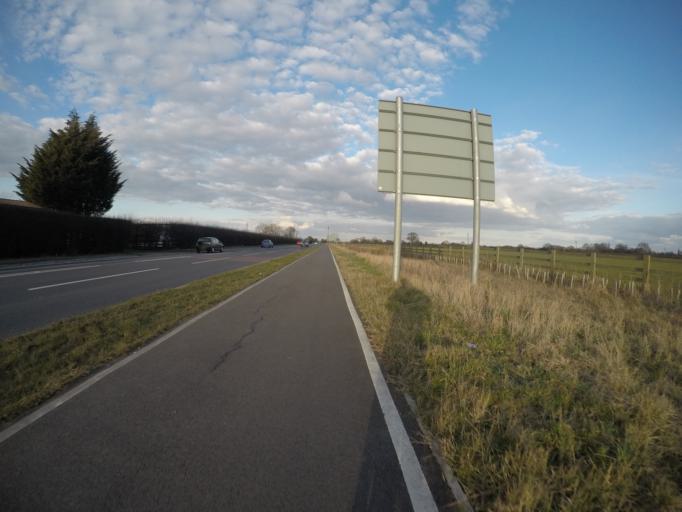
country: GB
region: England
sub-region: City of York
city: Wigginton
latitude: 53.9965
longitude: -1.0884
